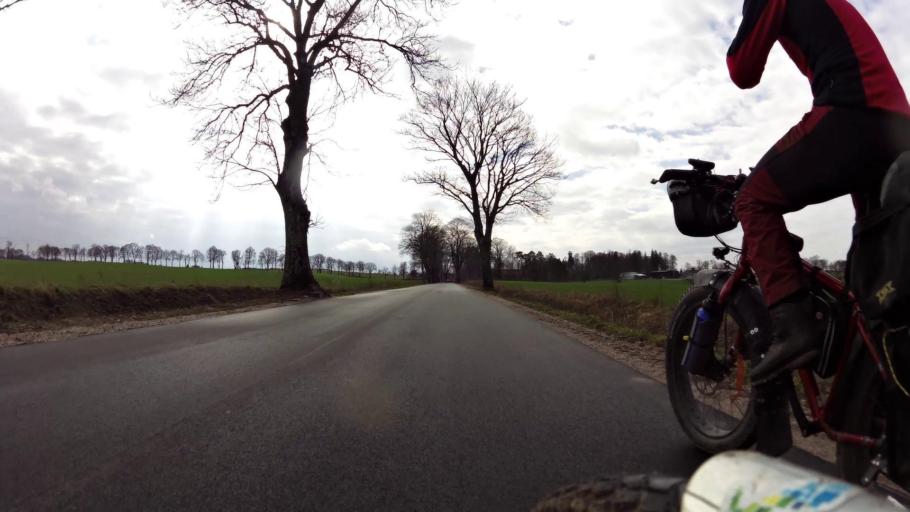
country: PL
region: Pomeranian Voivodeship
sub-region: Powiat bytowski
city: Kolczyglowy
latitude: 54.2230
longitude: 17.2402
